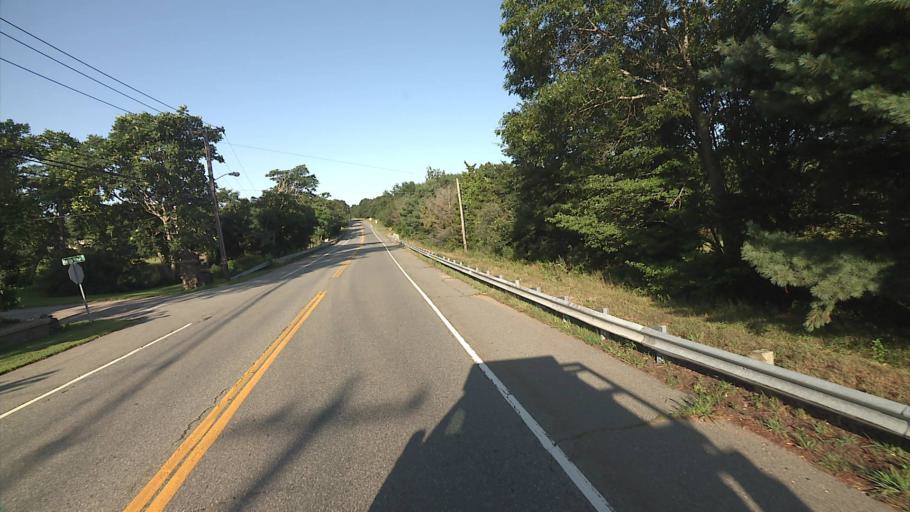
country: US
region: Connecticut
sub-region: New London County
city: Mystic
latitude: 41.3475
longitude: -71.9196
